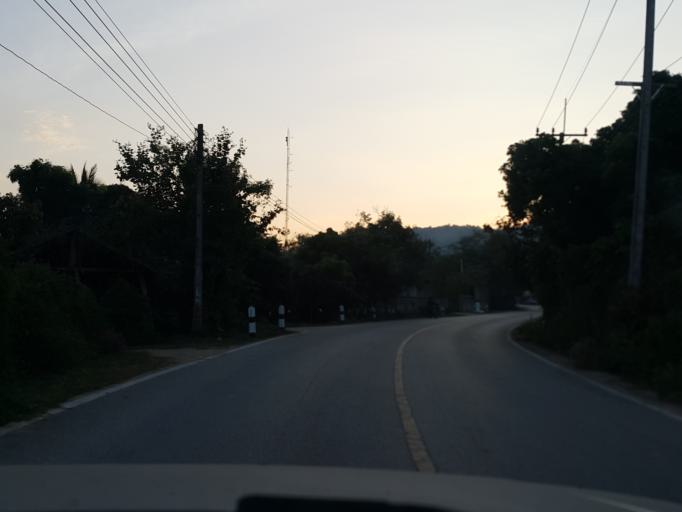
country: TH
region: Lamphun
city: Ban Thi
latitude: 18.5879
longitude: 99.2650
